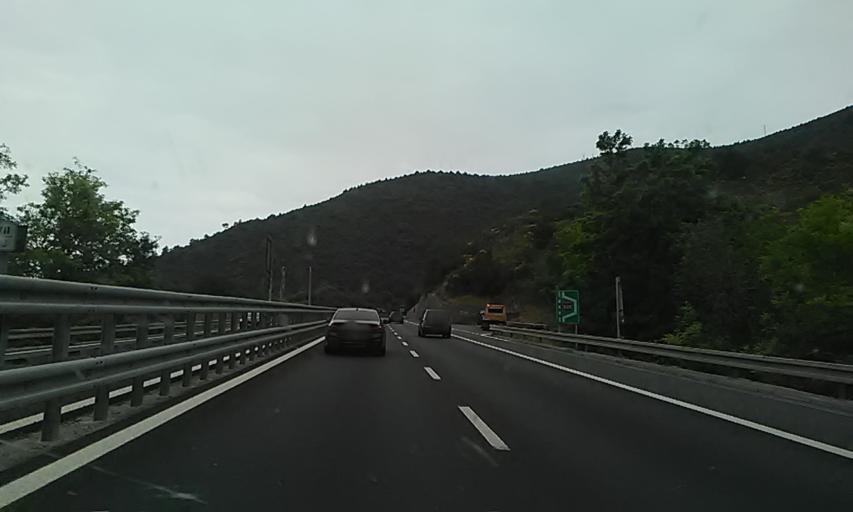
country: IT
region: Liguria
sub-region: Provincia di Savona
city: Borghetto Santo Spirito
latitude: 44.1136
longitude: 8.2292
